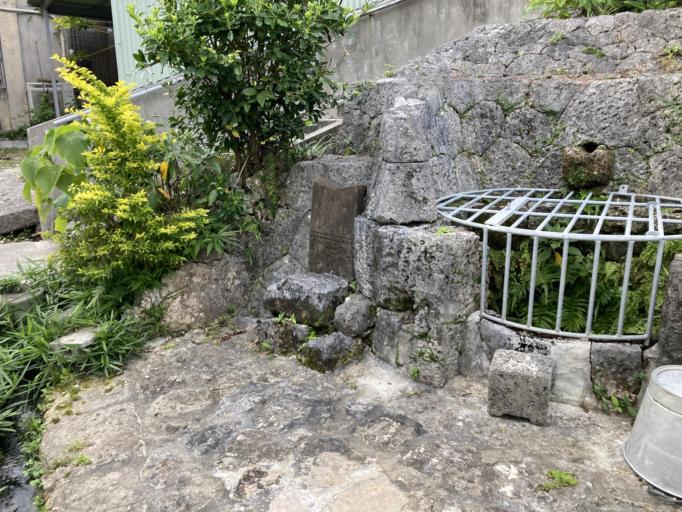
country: JP
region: Okinawa
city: Naha-shi
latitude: 26.2098
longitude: 127.7332
